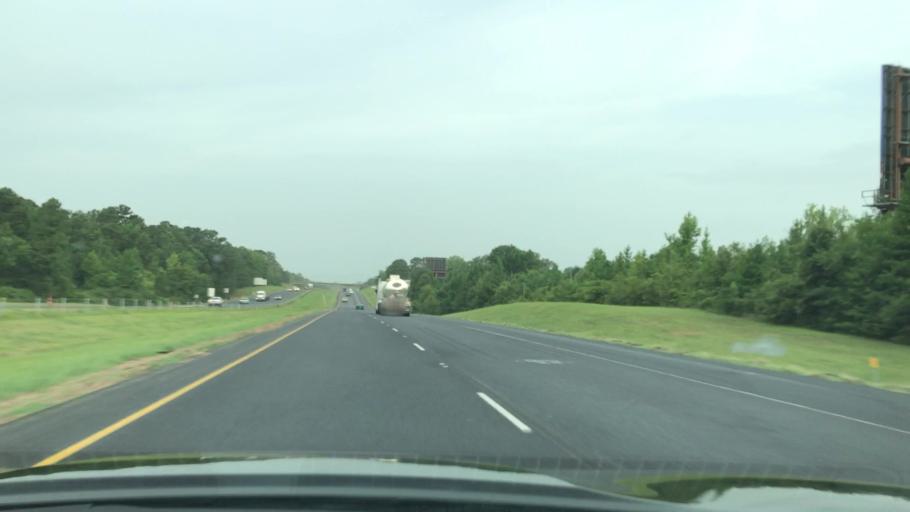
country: US
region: Louisiana
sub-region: Caddo Parish
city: Greenwood
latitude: 32.4518
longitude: -94.0025
